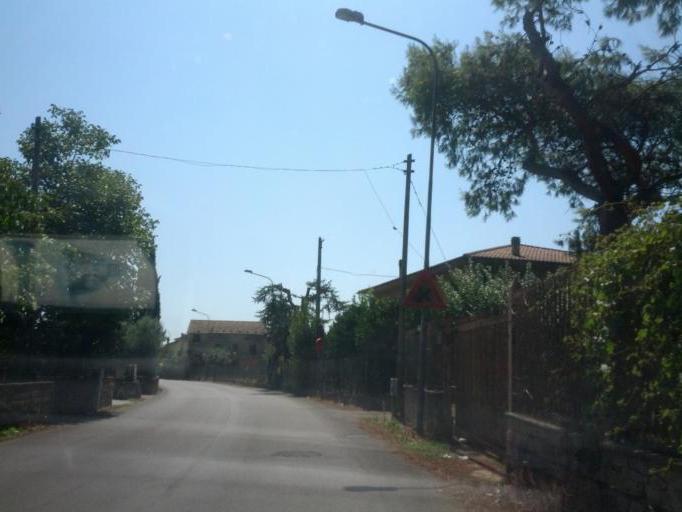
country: IT
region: Latium
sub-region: Provincia di Latina
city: Monte San Biagio
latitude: 41.3600
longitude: 13.3547
